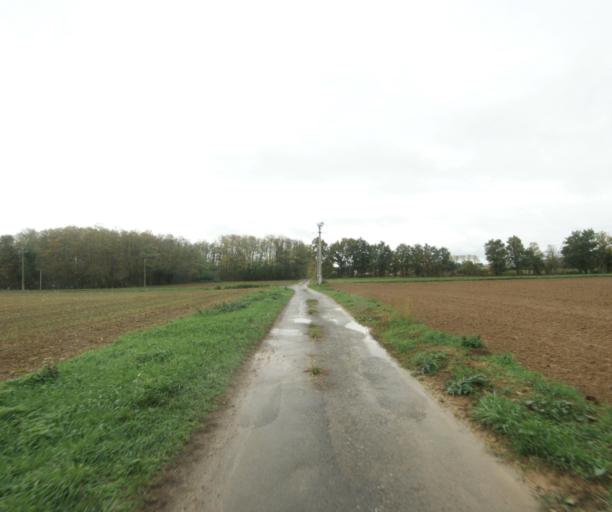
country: FR
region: Rhone-Alpes
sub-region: Departement de l'Ain
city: Pont-de-Vaux
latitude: 46.4861
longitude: 4.8797
